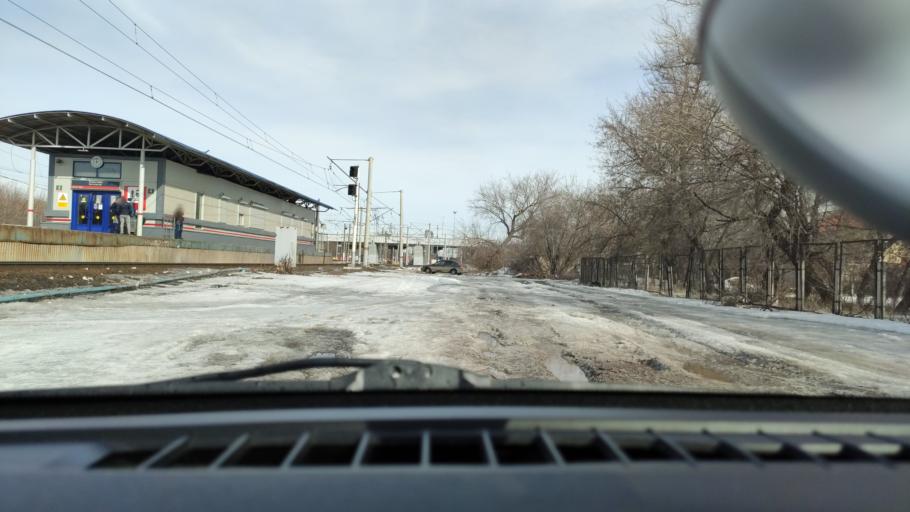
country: RU
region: Samara
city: Smyshlyayevka
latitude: 53.2193
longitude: 50.2862
